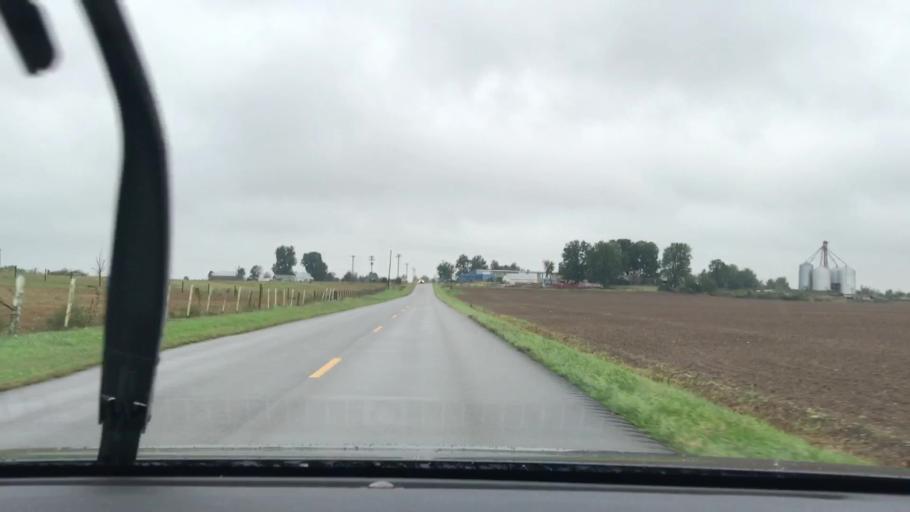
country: US
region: Kentucky
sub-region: Hopkins County
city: Madisonville
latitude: 37.3752
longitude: -87.3492
